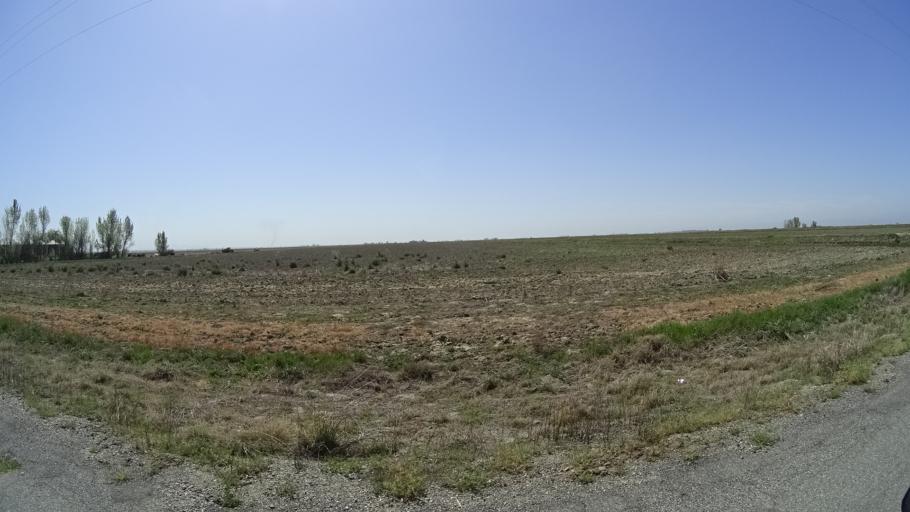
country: US
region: California
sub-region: Glenn County
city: Willows
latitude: 39.4931
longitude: -122.0804
